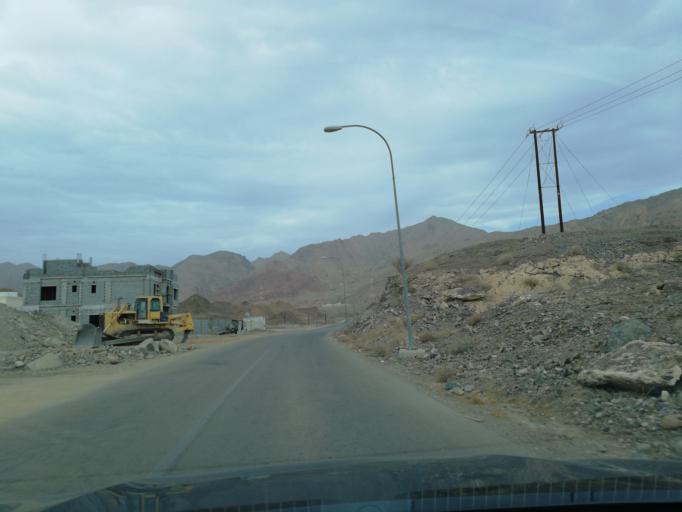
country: OM
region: Muhafazat Masqat
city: Bawshar
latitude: 23.4874
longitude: 58.3349
